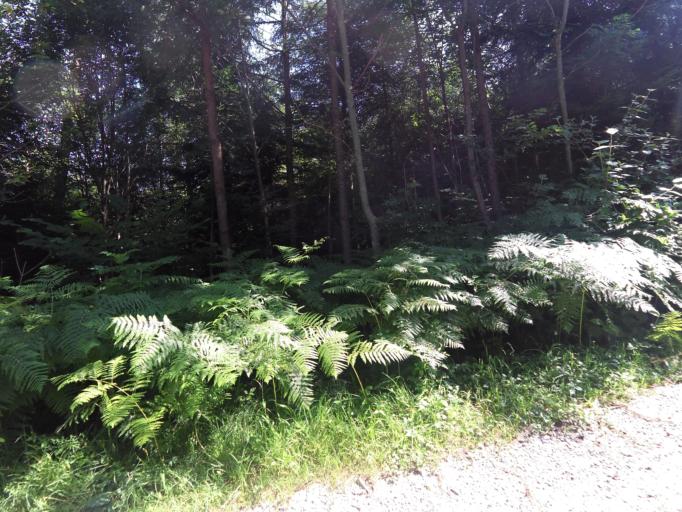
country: CH
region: Thurgau
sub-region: Frauenfeld District
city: Mullheim
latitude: 47.5744
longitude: 8.9896
